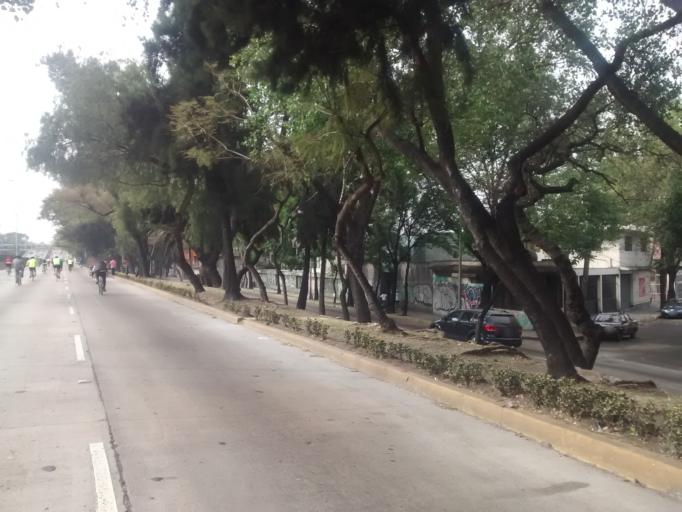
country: MX
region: Mexico City
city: Colonia Nativitas
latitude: 19.3647
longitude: -99.1277
